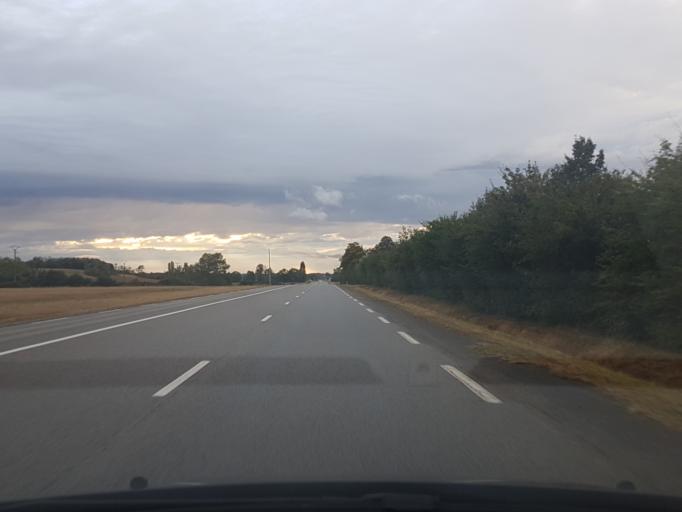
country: FR
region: Midi-Pyrenees
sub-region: Departement de l'Ariege
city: Mirepoix
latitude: 43.0744
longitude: 1.7852
